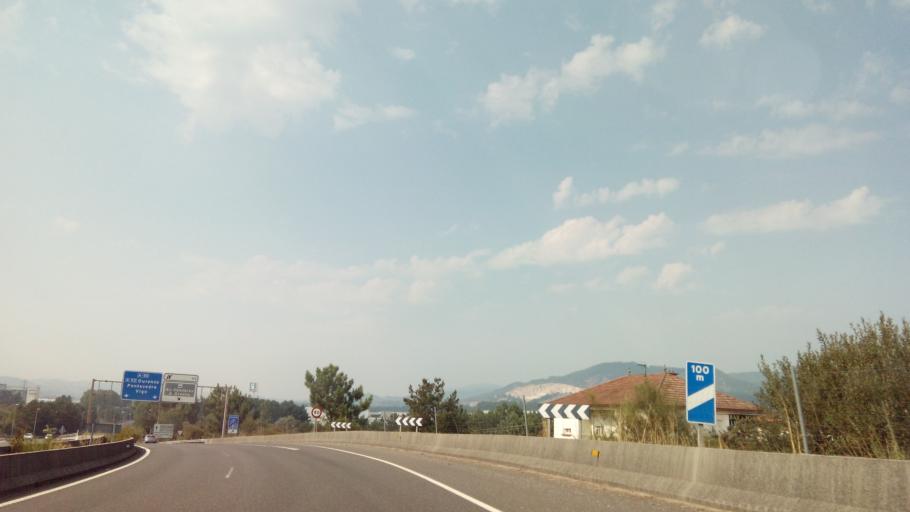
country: ES
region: Galicia
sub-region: Provincia de Pontevedra
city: Tui
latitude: 42.1016
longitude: -8.6200
